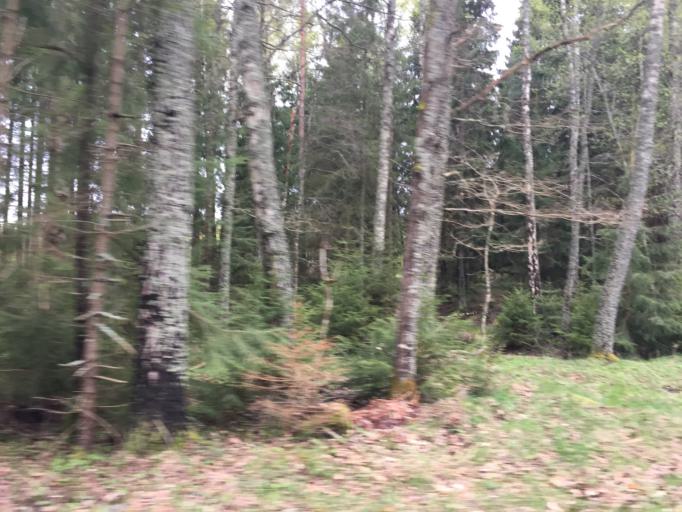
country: SE
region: Soedermanland
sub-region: Vingakers Kommun
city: Vingaker
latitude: 59.0089
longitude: 15.7343
